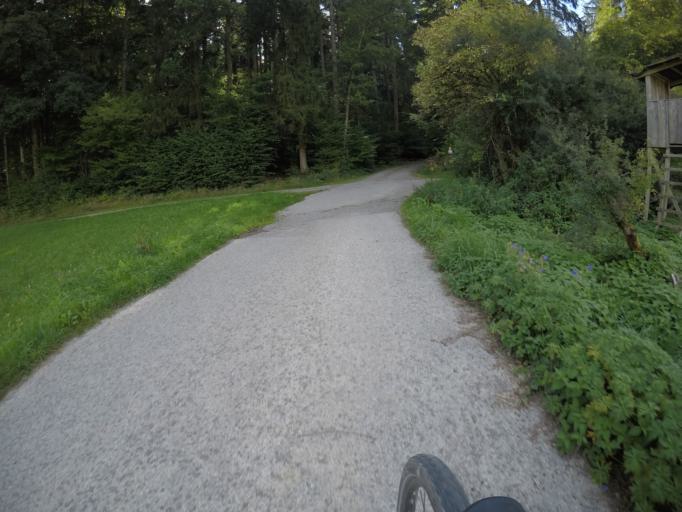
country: DE
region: Baden-Wuerttemberg
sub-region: Karlsruhe Region
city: Gechingen
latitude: 48.6817
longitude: 8.8218
